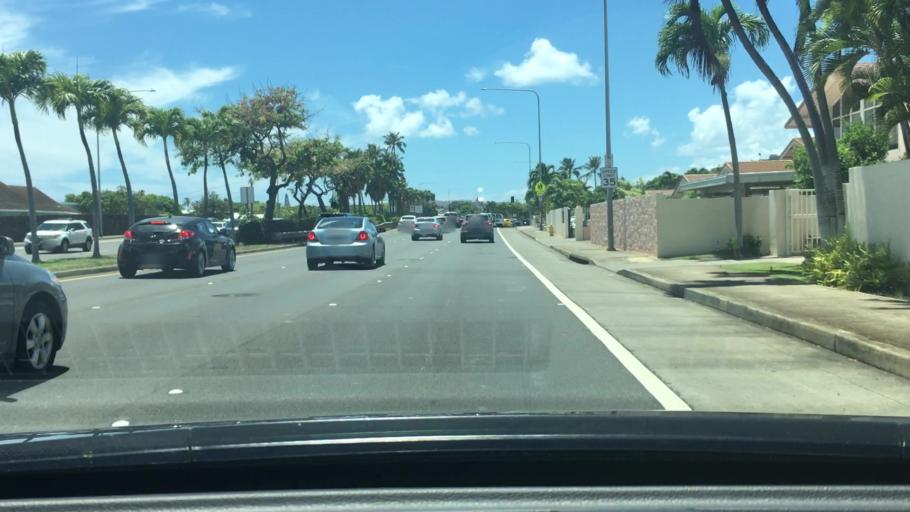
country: US
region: Hawaii
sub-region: Honolulu County
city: Waimanalo
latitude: 21.2787
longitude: -157.7499
